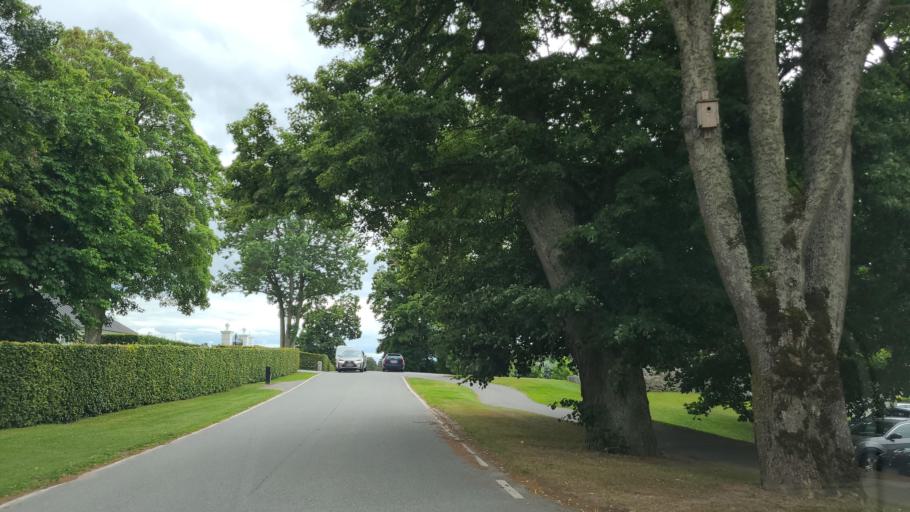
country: SE
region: Stockholm
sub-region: Upplands-Bro Kommun
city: Bro
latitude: 59.4968
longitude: 17.6251
